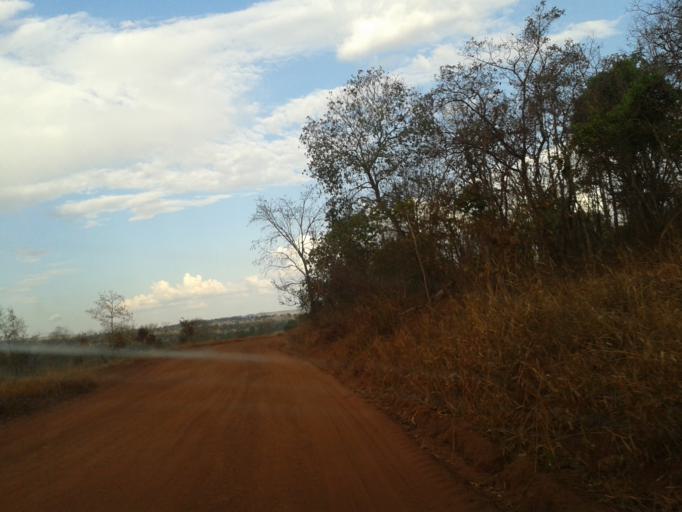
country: BR
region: Minas Gerais
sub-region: Santa Vitoria
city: Santa Vitoria
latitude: -19.1821
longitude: -49.8488
